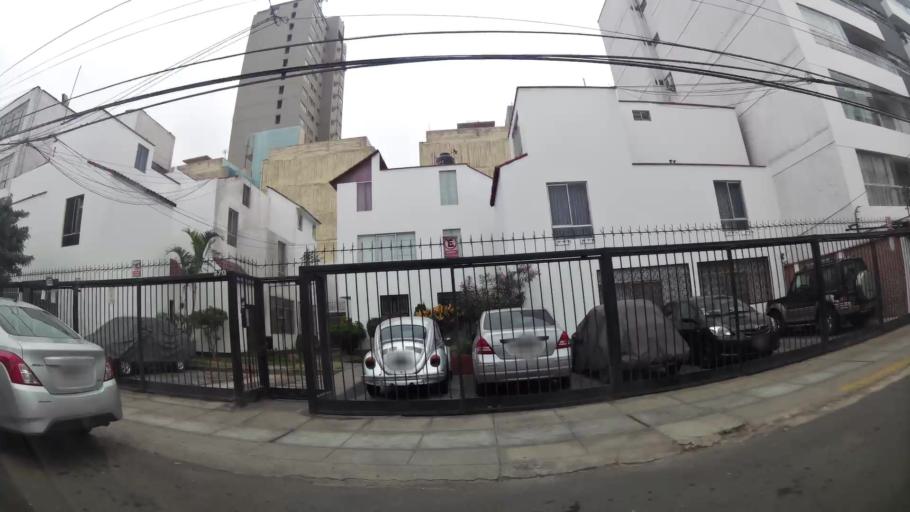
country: PE
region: Lima
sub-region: Lima
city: San Isidro
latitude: -12.1143
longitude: -77.0324
